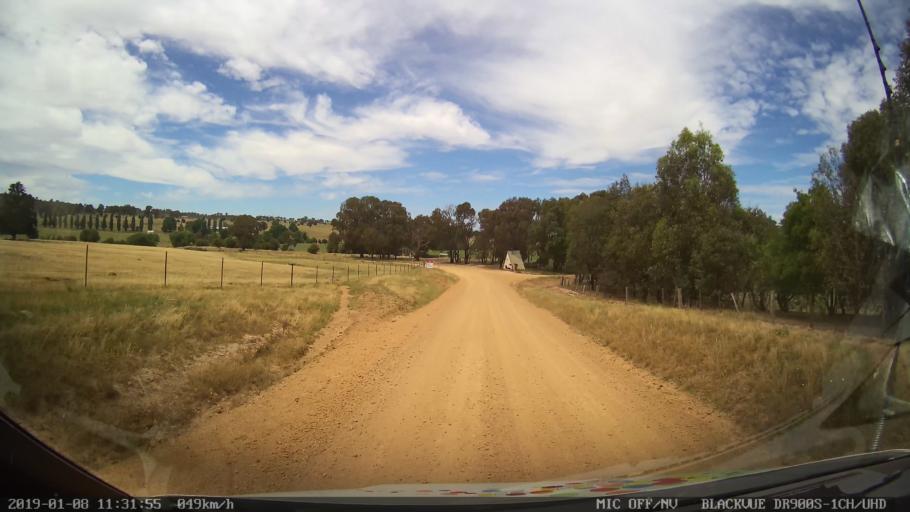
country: AU
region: New South Wales
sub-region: Guyra
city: Guyra
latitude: -30.3152
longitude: 151.5341
